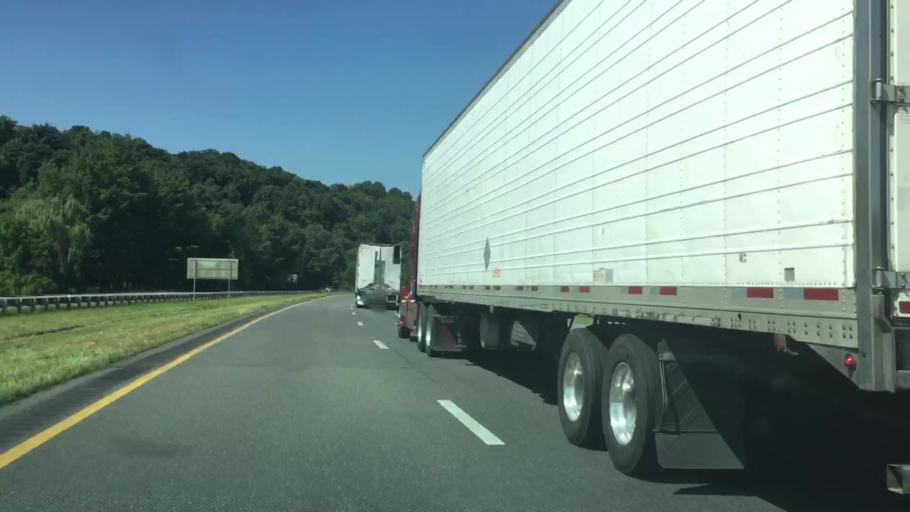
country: US
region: Virginia
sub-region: Smyth County
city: Adwolf
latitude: 36.8087
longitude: -81.6207
